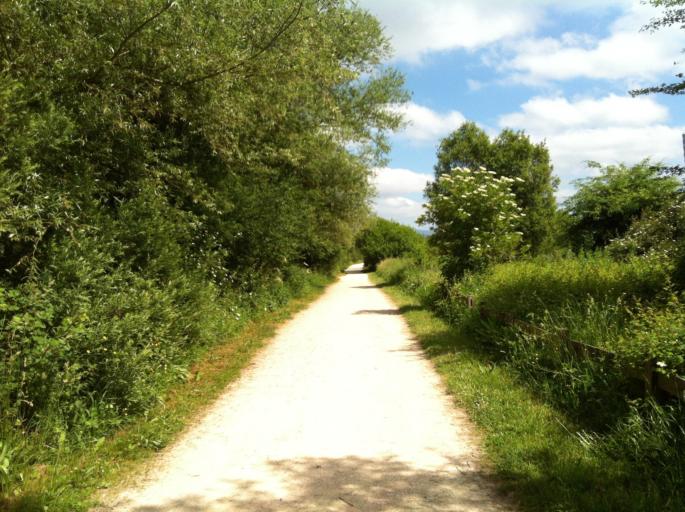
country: ES
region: Basque Country
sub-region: Provincia de Alava
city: Gasteiz / Vitoria
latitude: 42.8575
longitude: -2.6502
